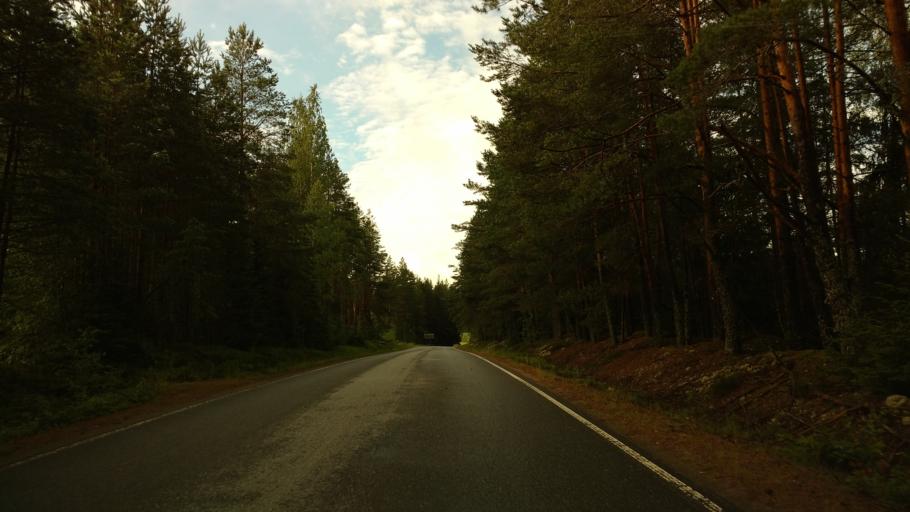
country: FI
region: Haeme
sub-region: Forssa
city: Ypaejae
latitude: 60.7508
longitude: 23.2054
